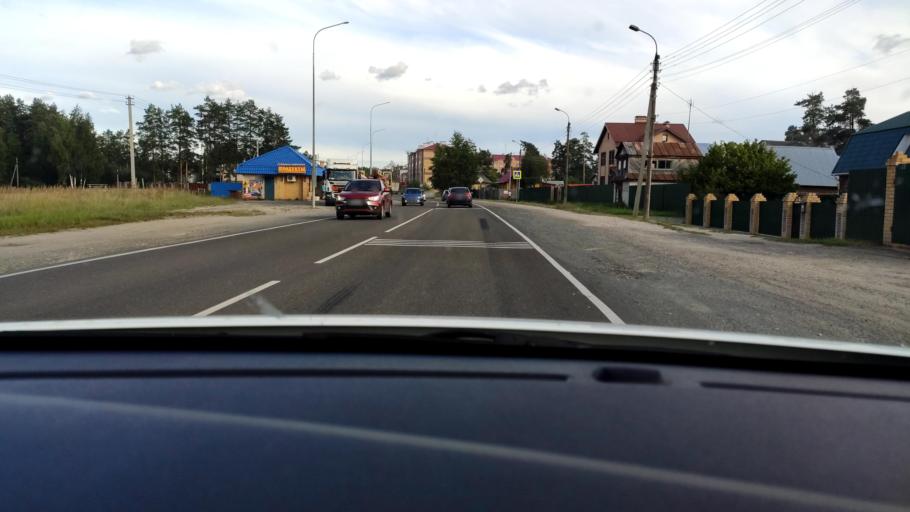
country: RU
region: Mariy-El
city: Suslonger
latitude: 56.3817
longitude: 48.1981
